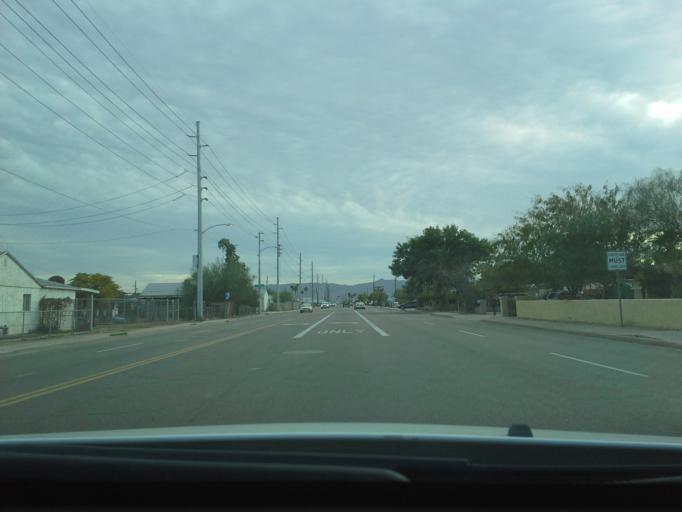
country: US
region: Arizona
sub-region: Maricopa County
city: Phoenix
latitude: 33.4483
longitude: -112.1176
